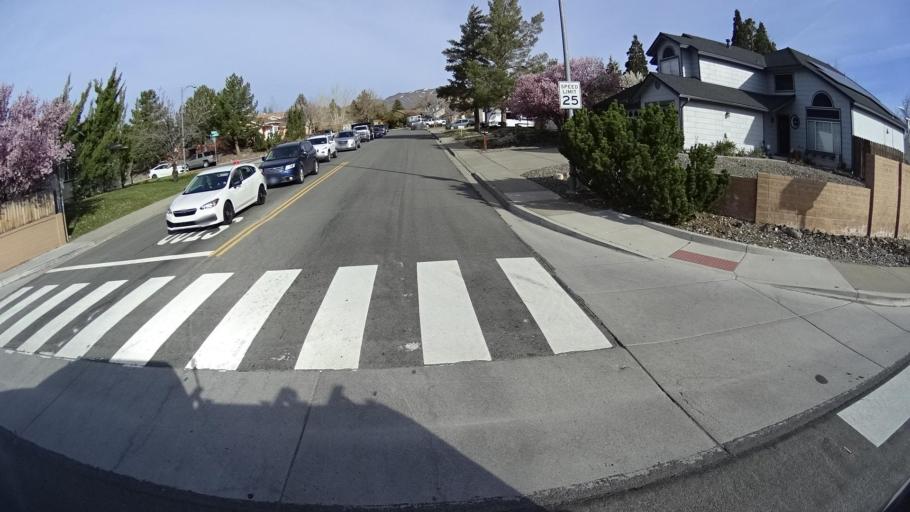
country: US
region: Nevada
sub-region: Washoe County
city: Mogul
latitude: 39.5264
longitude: -119.8882
